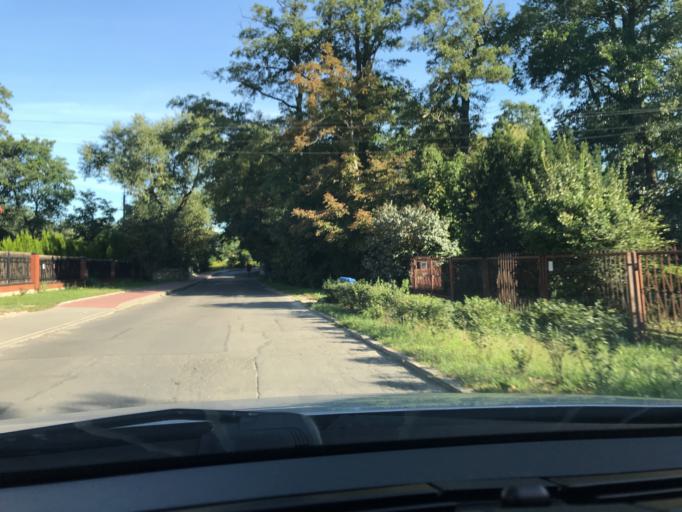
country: PL
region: Masovian Voivodeship
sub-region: Powiat pruszkowski
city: Piastow
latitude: 52.1705
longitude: 20.8411
